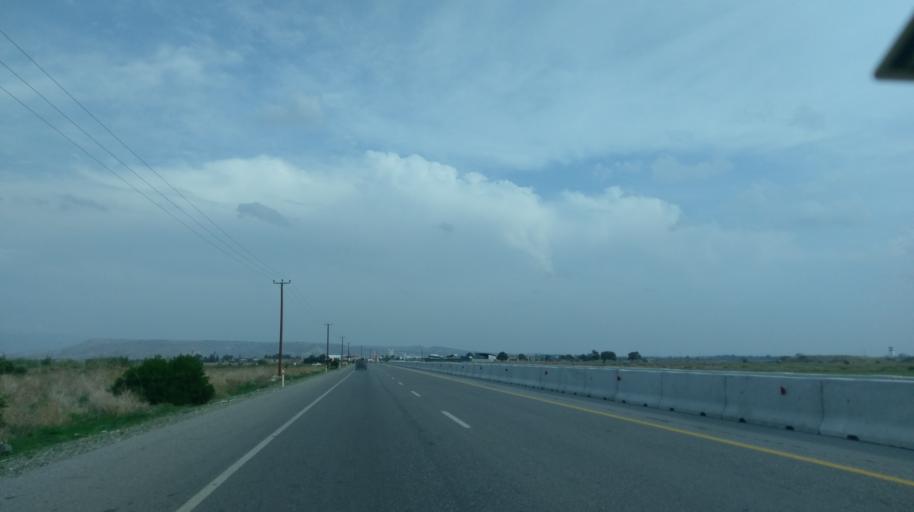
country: CY
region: Lefkosia
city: Morfou
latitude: 35.1987
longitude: 33.0245
